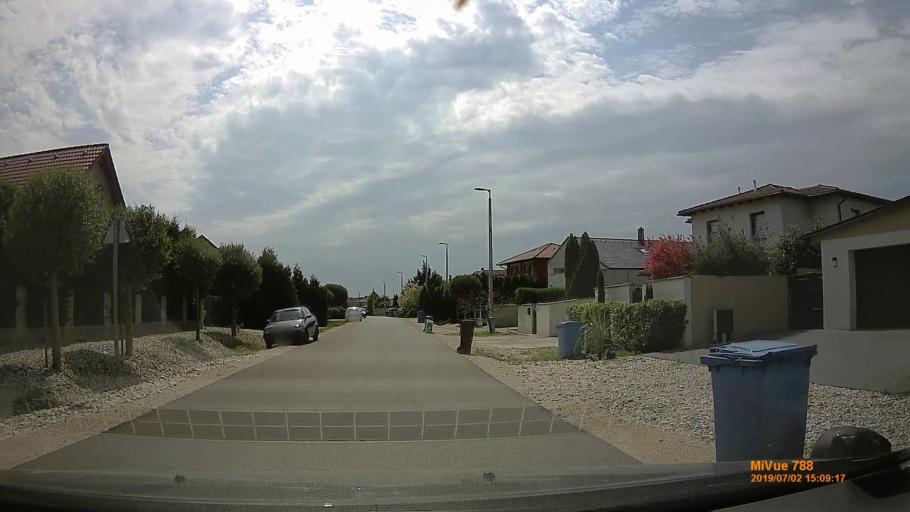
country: HU
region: Gyor-Moson-Sopron
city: Mosonmagyarovar
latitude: 47.8907
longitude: 17.2924
